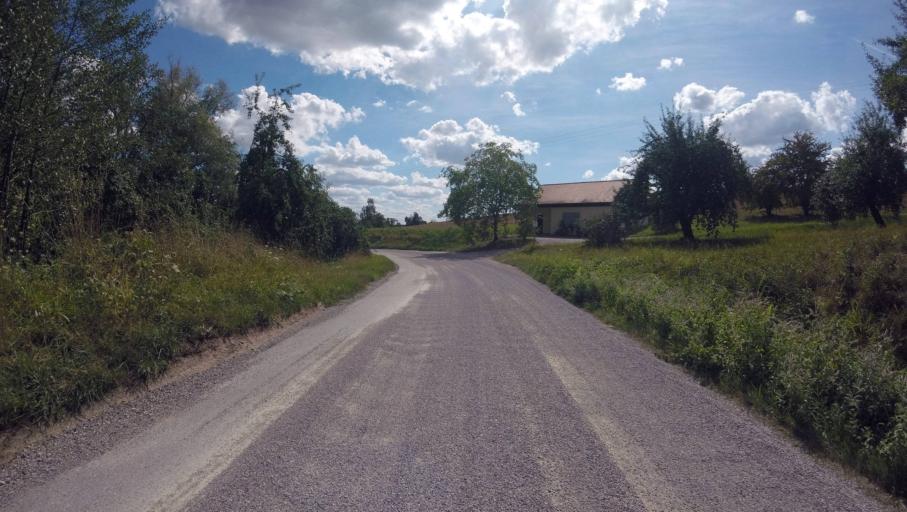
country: DE
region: Baden-Wuerttemberg
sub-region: Regierungsbezirk Stuttgart
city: Oberstenfeld
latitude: 49.0040
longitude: 9.3644
